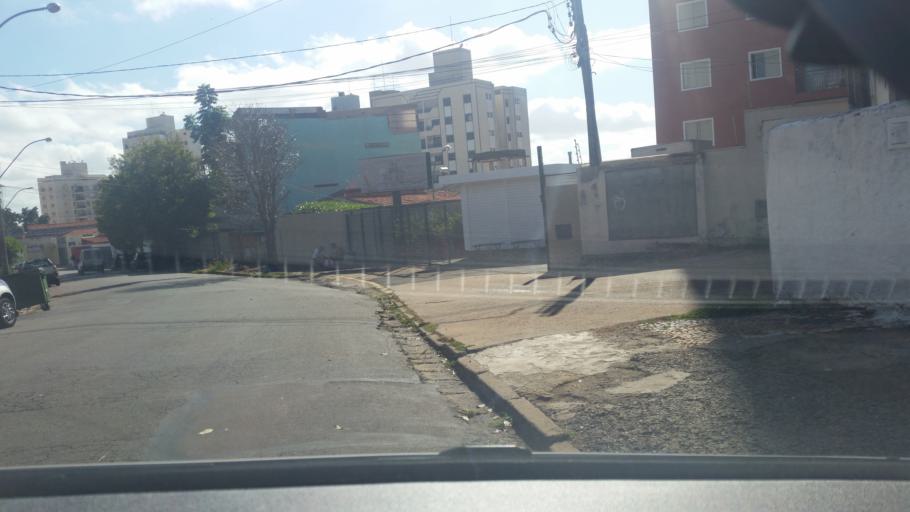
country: BR
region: Sao Paulo
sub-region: Campinas
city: Campinas
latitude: -22.8830
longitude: -47.0681
